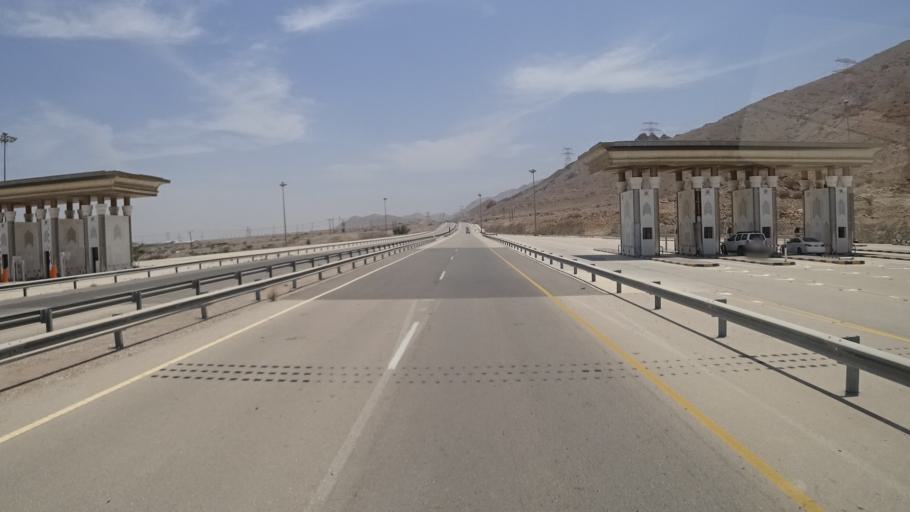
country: OM
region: Ash Sharqiyah
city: Sur
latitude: 22.6681
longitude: 59.3893
